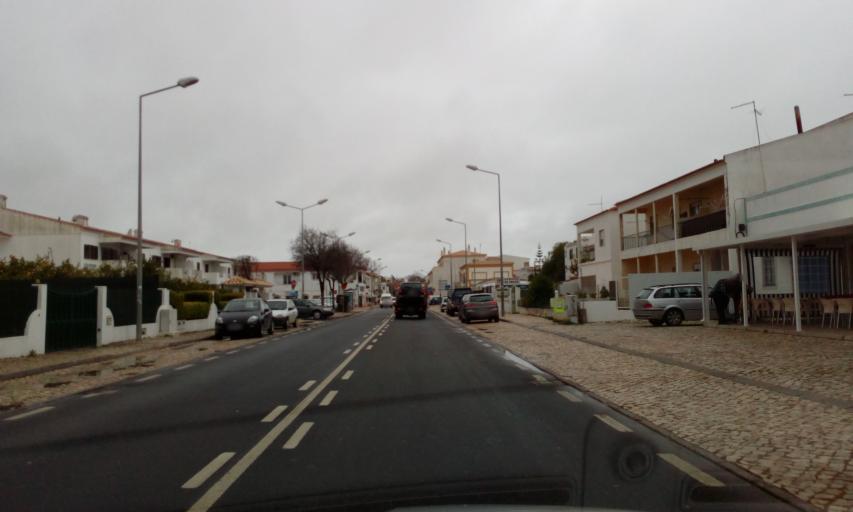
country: PT
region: Faro
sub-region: Albufeira
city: Ferreiras
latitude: 37.1267
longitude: -8.2413
